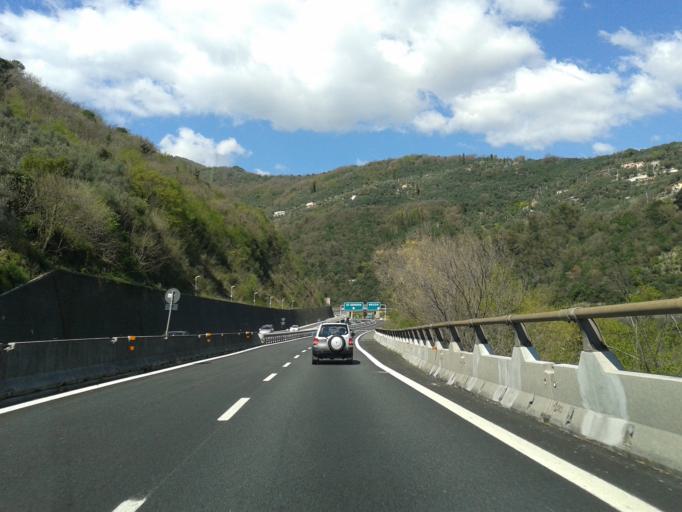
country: IT
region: Liguria
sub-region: Provincia di Genova
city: Avegno
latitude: 44.3748
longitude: 9.1491
